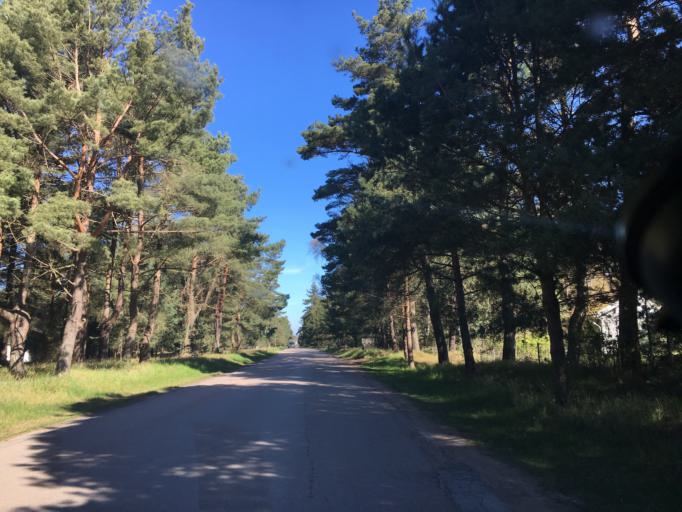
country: SE
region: Skane
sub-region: Vellinge Kommun
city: Ljunghusen
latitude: 55.3994
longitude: 12.9221
